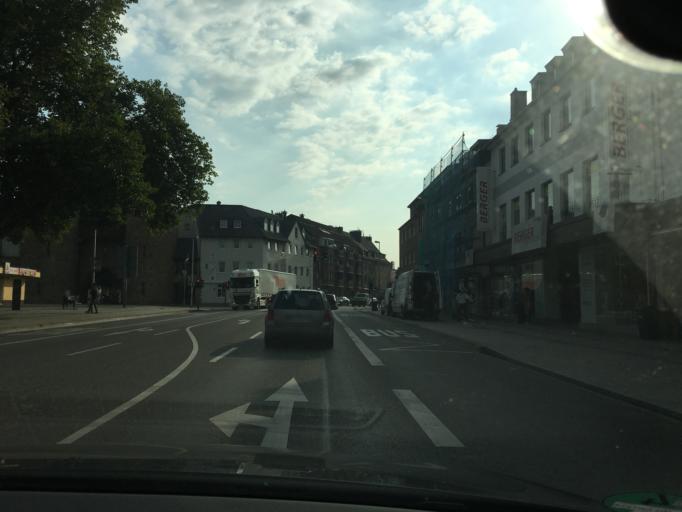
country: DE
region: North Rhine-Westphalia
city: Julich
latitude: 50.9202
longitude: 6.3550
